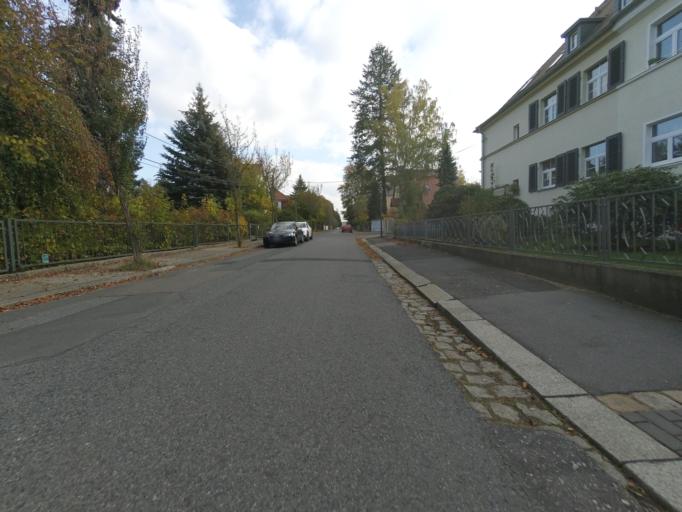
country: DE
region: Saxony
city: Albertstadt
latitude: 51.0653
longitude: 13.8426
